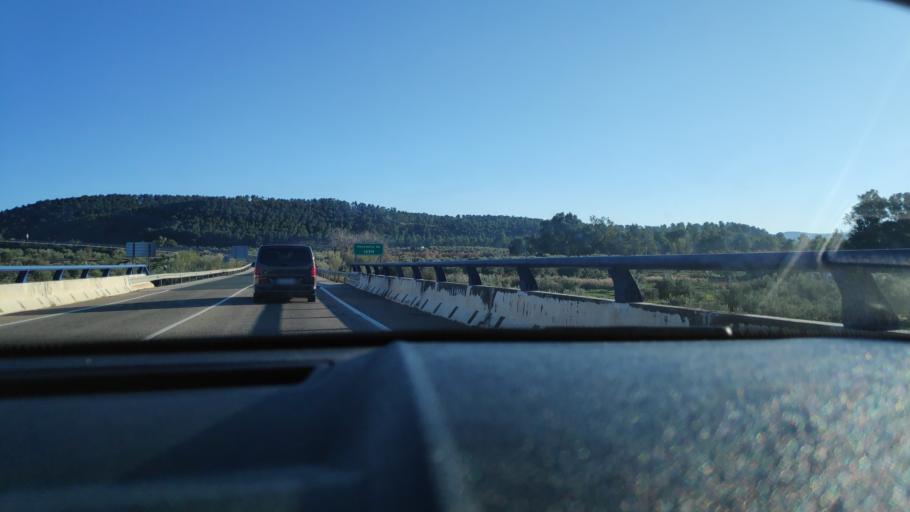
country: ES
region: Andalusia
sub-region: Province of Cordoba
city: Fuente-Tojar
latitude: 37.5780
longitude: -4.1593
